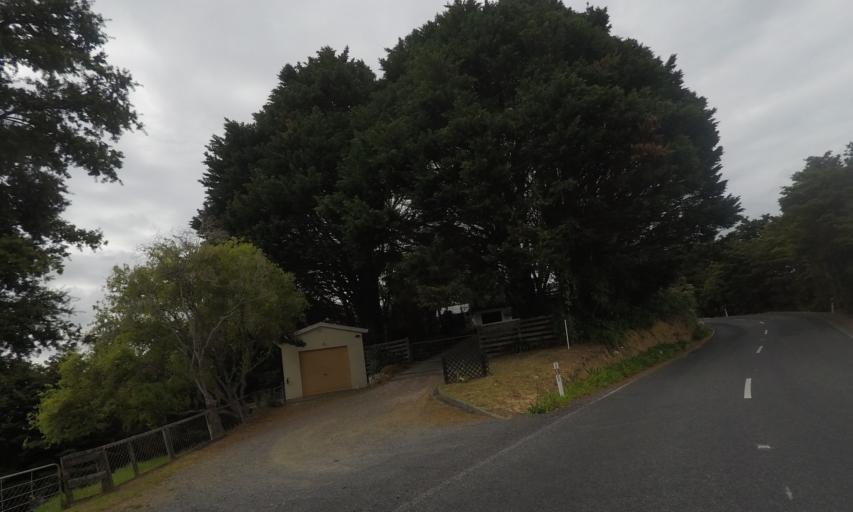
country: NZ
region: Northland
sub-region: Whangarei
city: Whangarei
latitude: -35.7592
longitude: 174.4551
